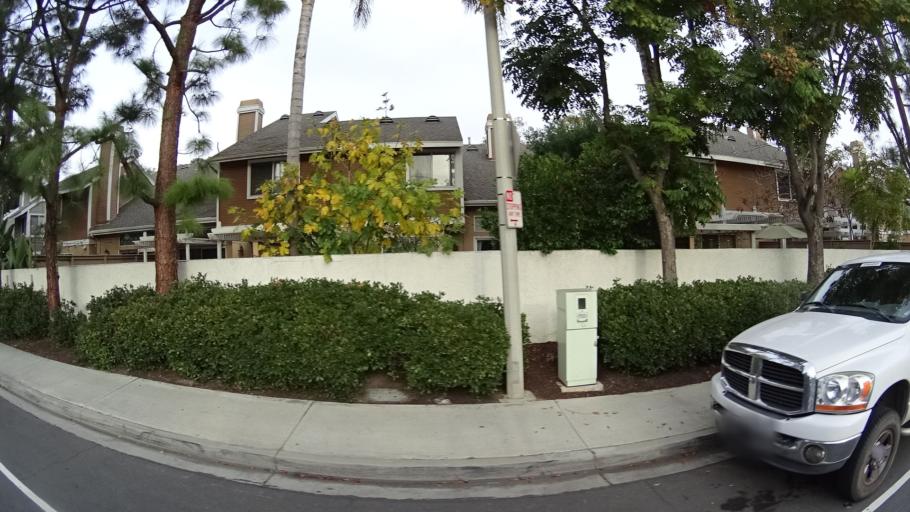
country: US
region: California
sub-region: Orange County
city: Laguna Woods
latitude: 33.5910
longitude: -117.7203
